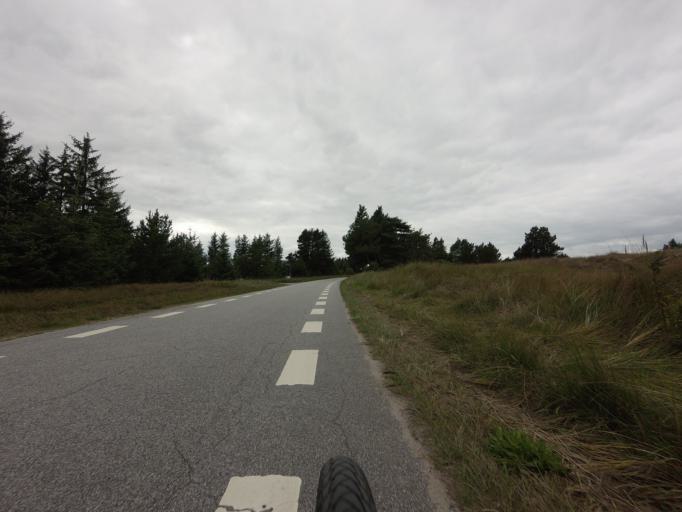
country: DK
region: North Denmark
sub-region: Hjorring Kommune
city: Sindal
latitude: 57.5883
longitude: 10.2162
